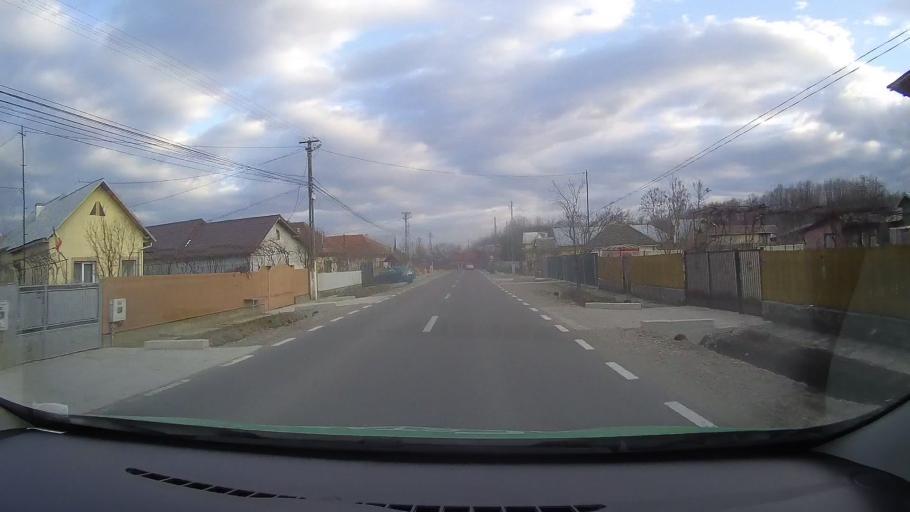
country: RO
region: Dambovita
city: Ion Luca Caragiale
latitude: 44.9156
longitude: 25.6910
